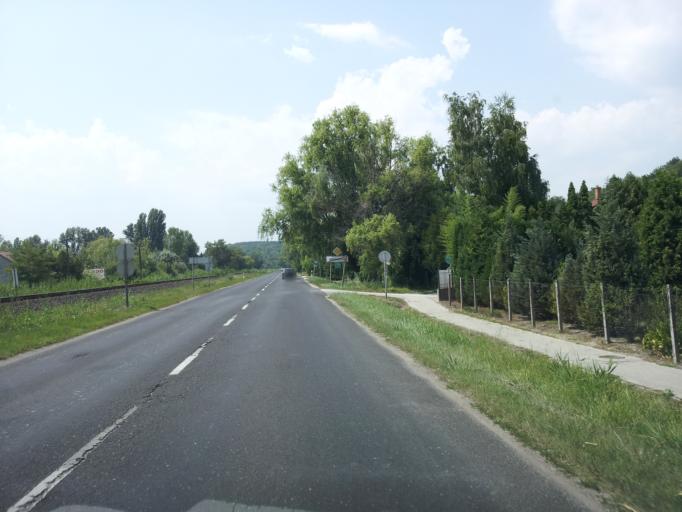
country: HU
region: Veszprem
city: Balatonkenese
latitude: 47.0350
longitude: 18.0904
